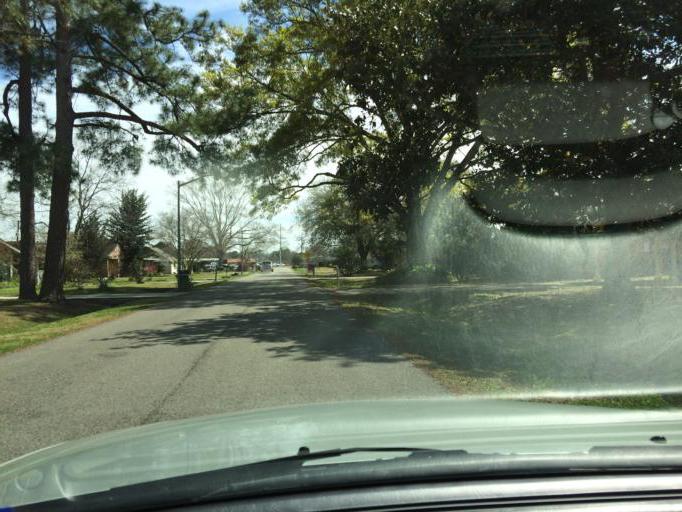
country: US
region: Louisiana
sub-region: Lafayette Parish
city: Lafayette
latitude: 30.2008
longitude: -92.0574
